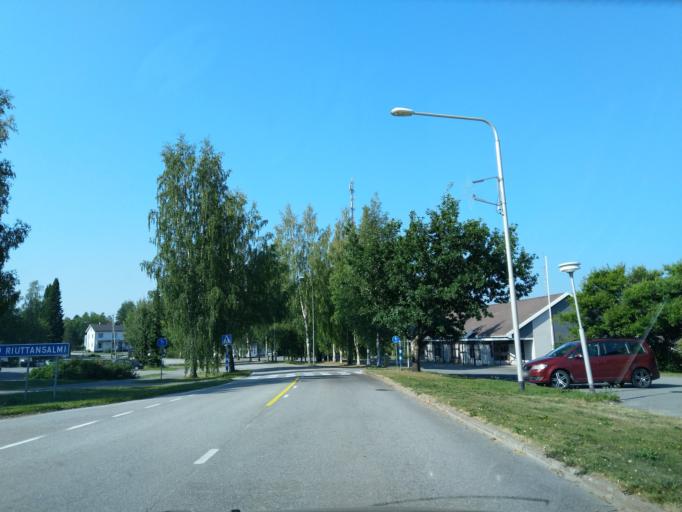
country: FI
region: Satakunta
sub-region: Pori
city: Pomarkku
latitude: 61.6935
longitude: 22.0086
